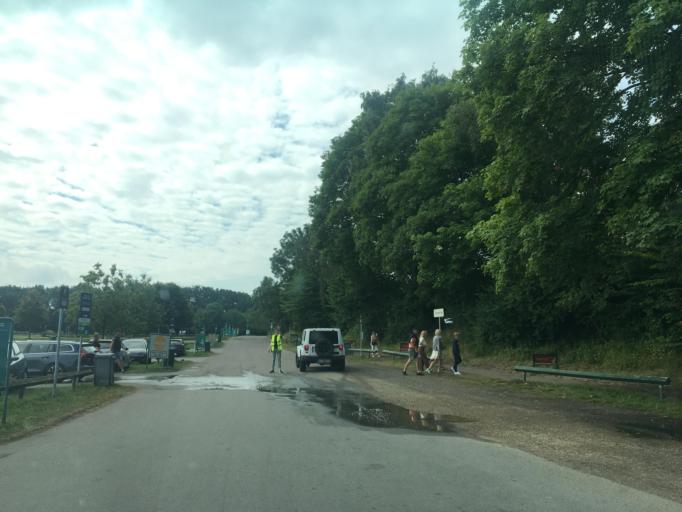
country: DK
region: Capital Region
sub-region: Gentofte Kommune
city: Charlottenlund
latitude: 55.7738
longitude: 12.5770
